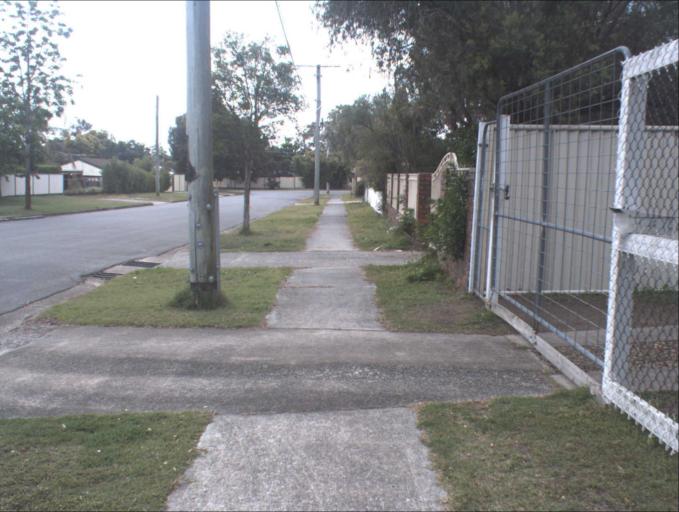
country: AU
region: Queensland
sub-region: Logan
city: Logan Reserve
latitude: -27.6815
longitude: 153.0831
